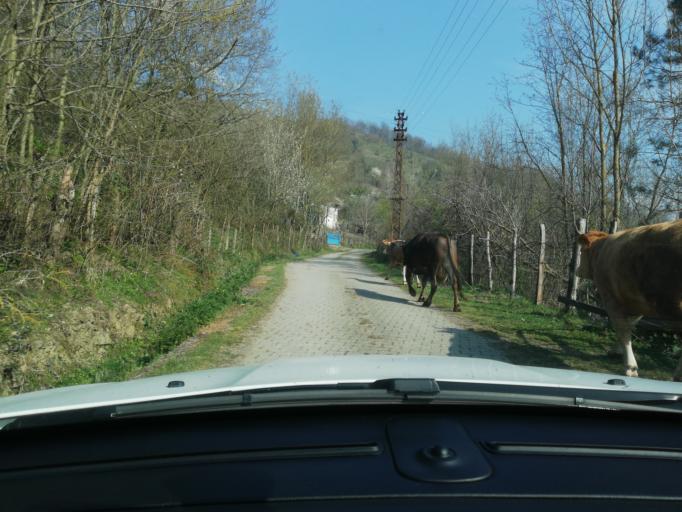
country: TR
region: Karabuk
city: Yenice
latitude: 41.2692
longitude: 32.3603
